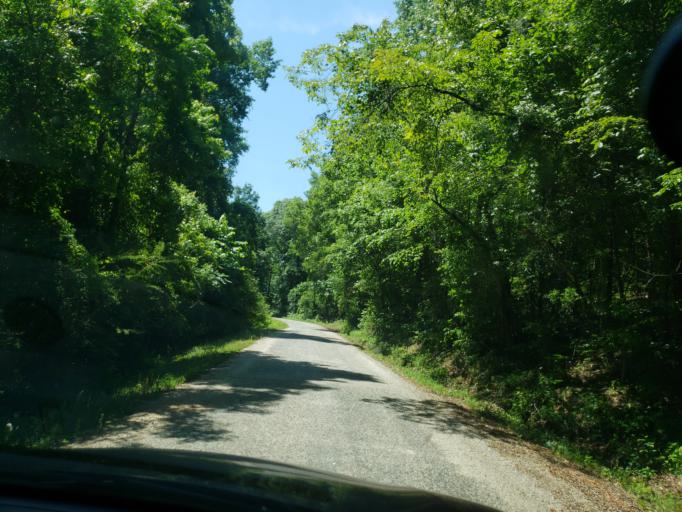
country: US
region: Alabama
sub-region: Elmore County
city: Tallassee
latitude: 32.5929
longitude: -85.8765
